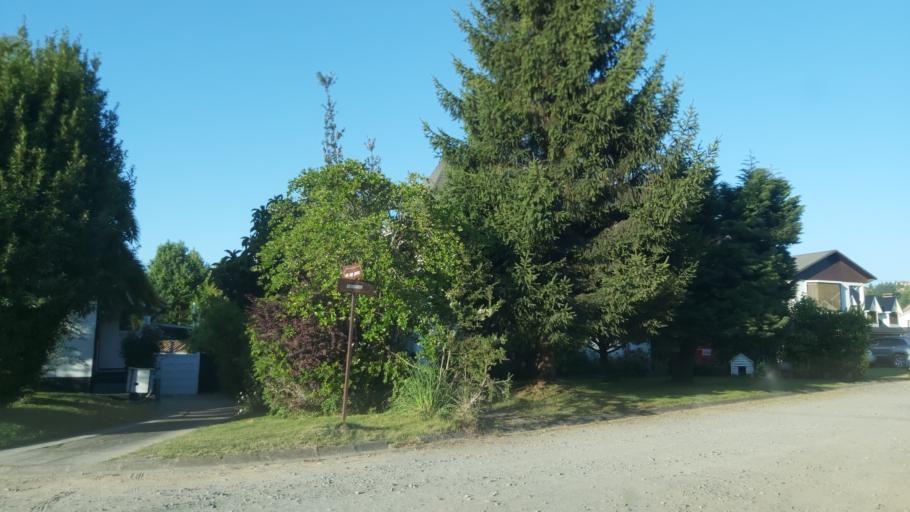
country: CL
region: Biobio
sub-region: Provincia de Concepcion
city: Tome
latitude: -36.5314
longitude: -72.9325
